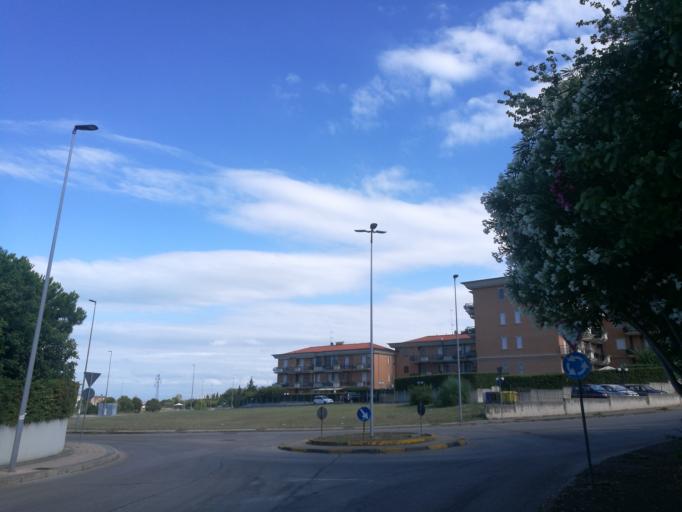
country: IT
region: Molise
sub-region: Provincia di Campobasso
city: Termoli
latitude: 41.9823
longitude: 14.9829
